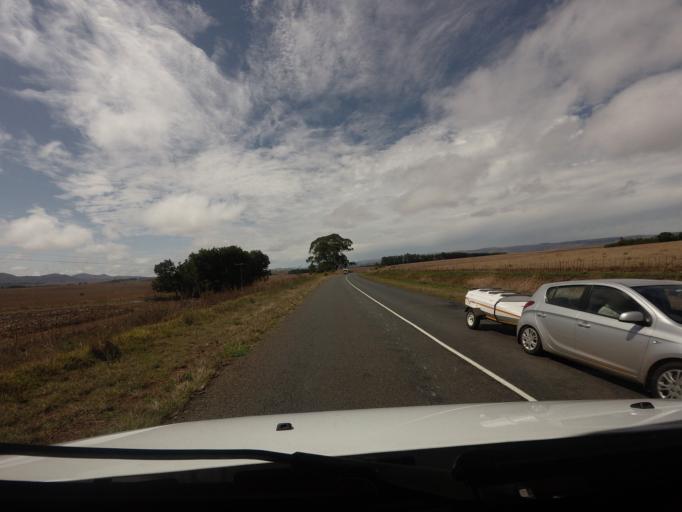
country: ZA
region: Mpumalanga
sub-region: Ehlanzeni District
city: Lydenburg
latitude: -25.1643
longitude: 30.3769
